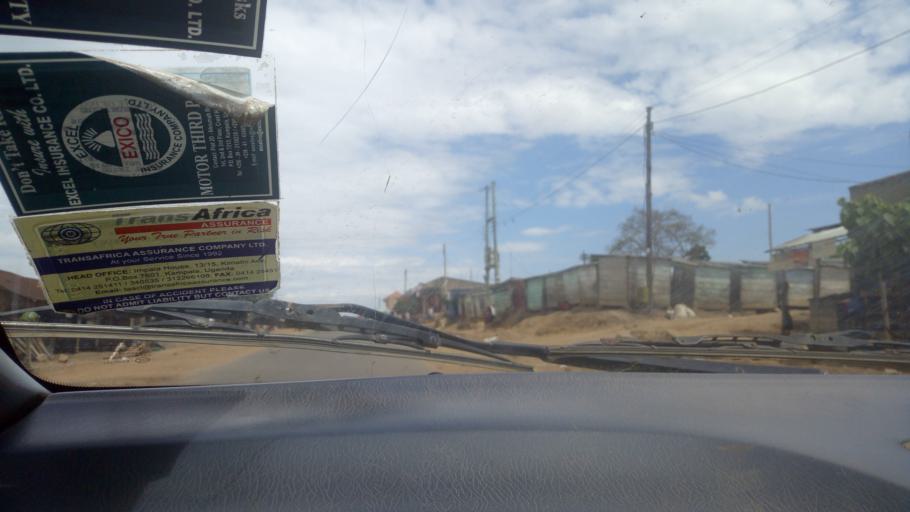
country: UG
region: Western Region
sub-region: Mbarara District
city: Bwizibwera
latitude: -0.4088
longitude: 30.5685
